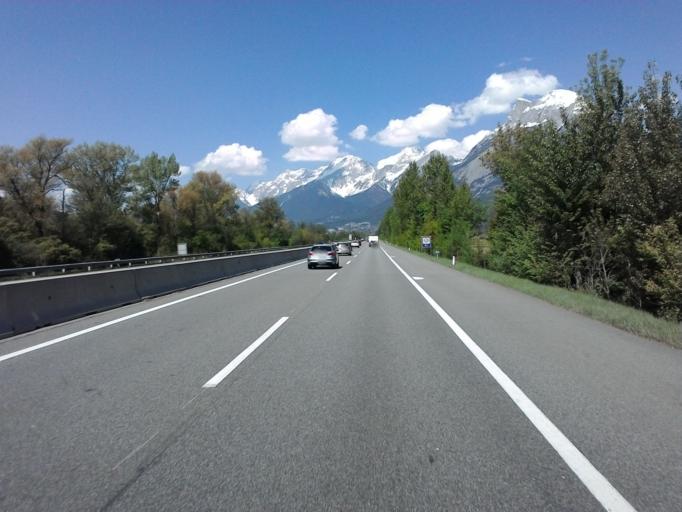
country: AT
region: Tyrol
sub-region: Politischer Bezirk Innsbruck Land
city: Polling in Tirol
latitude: 47.2896
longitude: 11.1518
